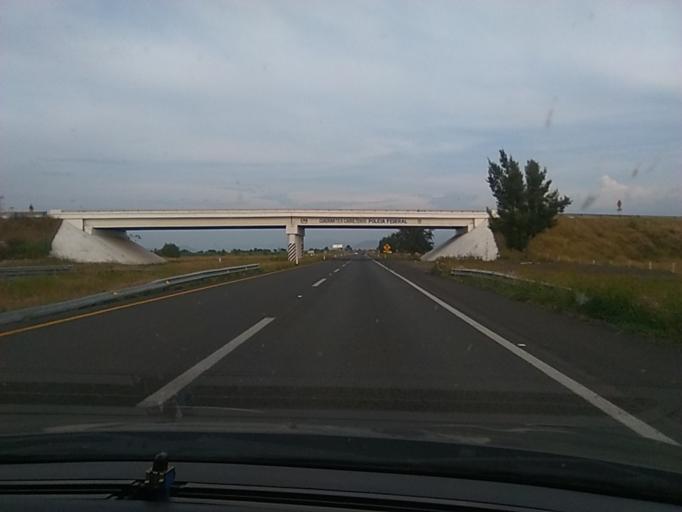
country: MX
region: Michoacan
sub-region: Alvaro Obregon
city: Lazaro Cardenas (La Purisima)
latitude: 19.8914
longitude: -101.0128
